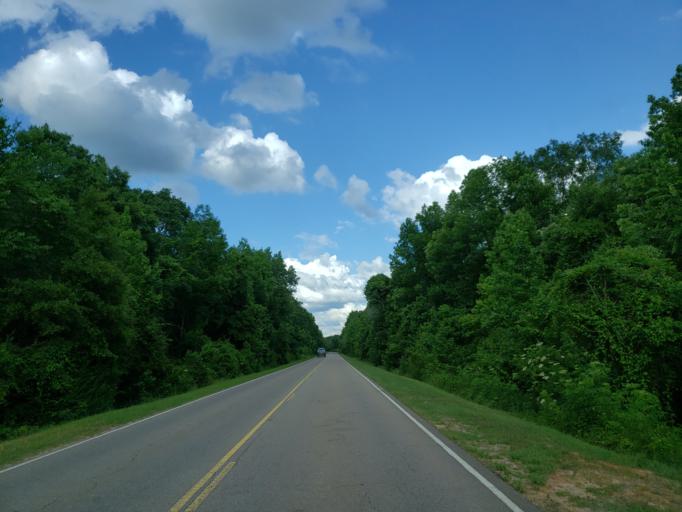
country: US
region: Mississippi
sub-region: Forrest County
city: Petal
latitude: 31.2615
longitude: -89.2235
